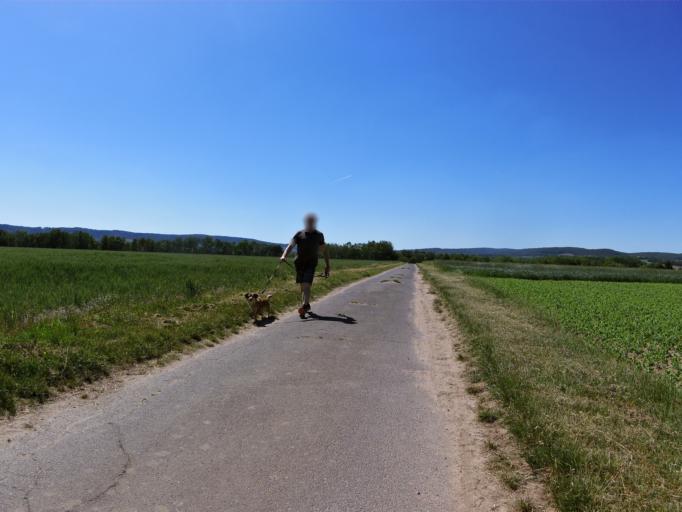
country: DE
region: Thuringia
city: Dankmarshausen
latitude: 50.9406
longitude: 10.0332
